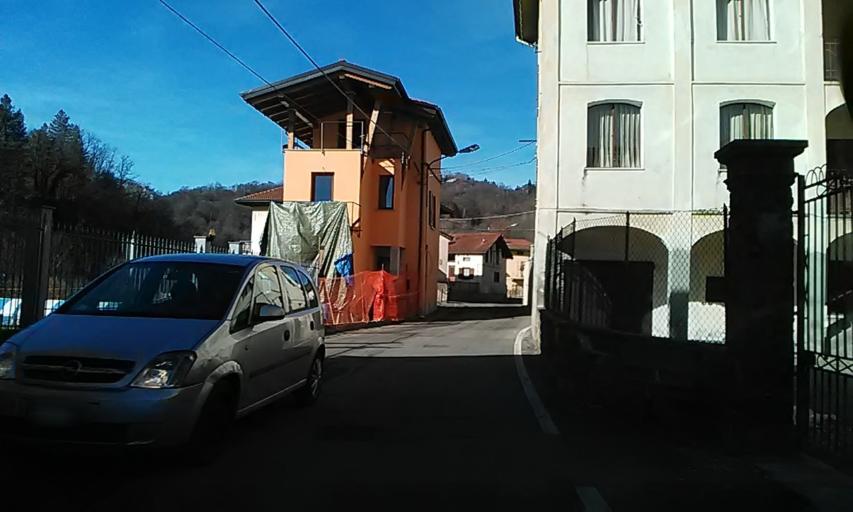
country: IT
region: Piedmont
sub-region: Provincia di Vercelli
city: Borgosesia
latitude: 45.7296
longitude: 8.2998
